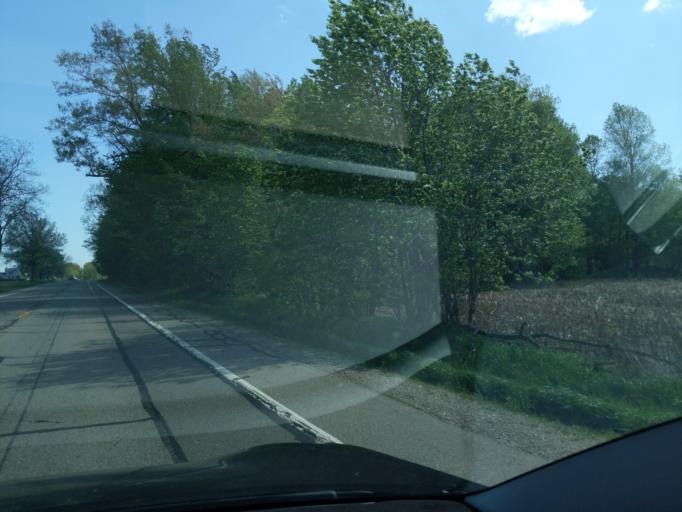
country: US
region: Michigan
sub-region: Kent County
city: Lowell
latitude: 42.8690
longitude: -85.3710
